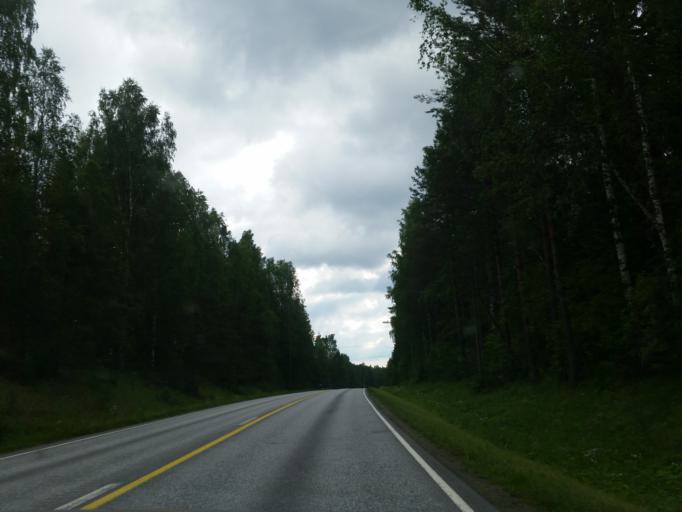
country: FI
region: Northern Savo
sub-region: Kuopio
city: Karttula
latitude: 62.8675
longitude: 27.1607
